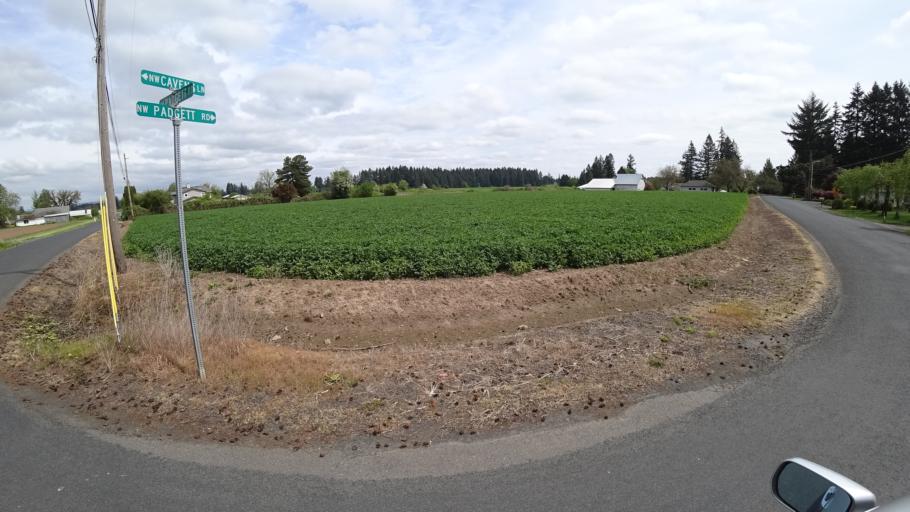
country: US
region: Oregon
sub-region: Washington County
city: Hillsboro
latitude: 45.5327
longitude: -123.0108
